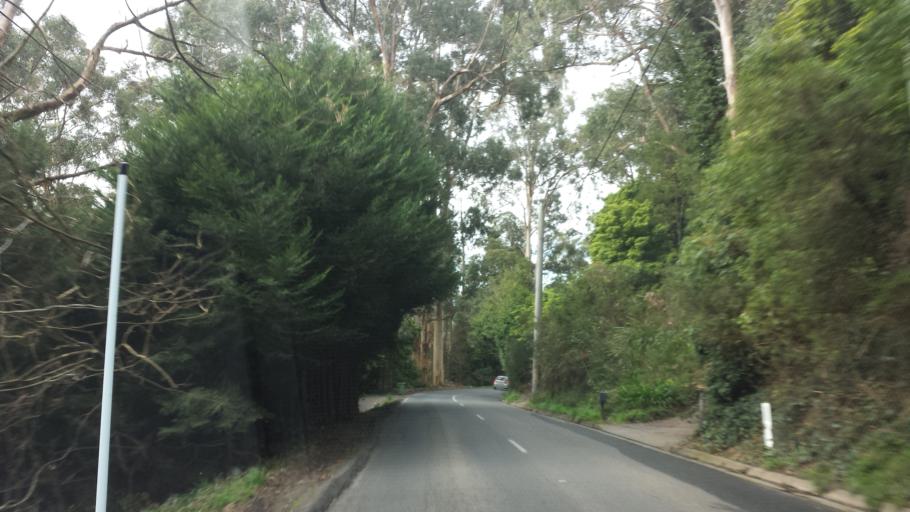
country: AU
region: Victoria
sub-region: Yarra Ranges
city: Kallista
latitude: -37.8862
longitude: 145.3828
